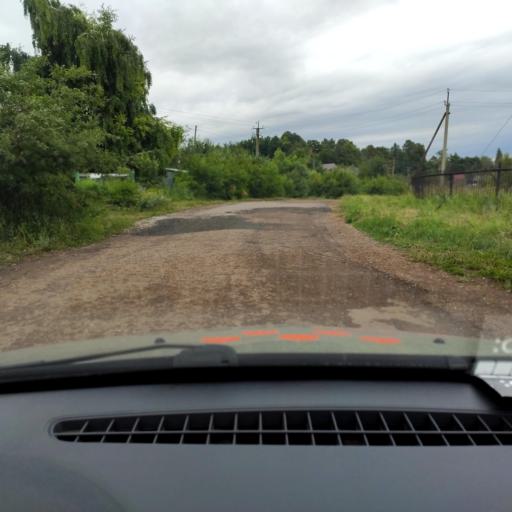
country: RU
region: Bashkortostan
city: Iglino
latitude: 54.8851
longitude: 56.2585
